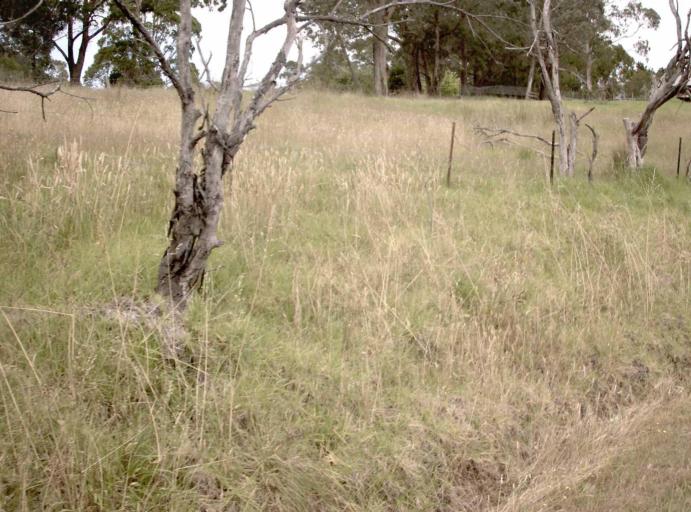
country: AU
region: Victoria
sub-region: Latrobe
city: Traralgon
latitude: -38.1342
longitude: 146.4752
